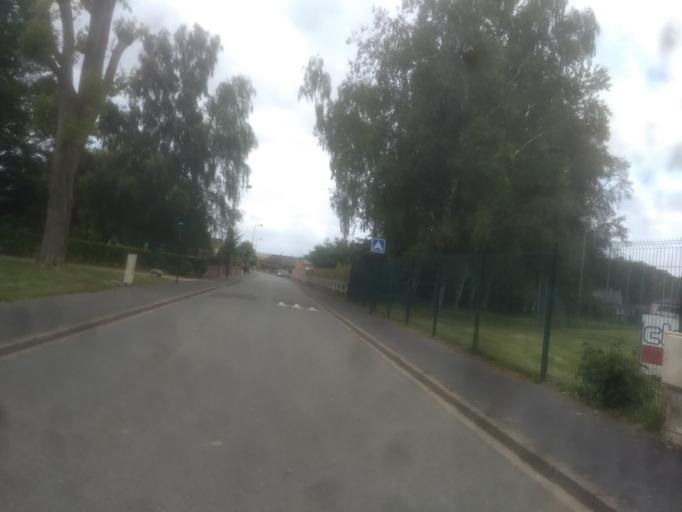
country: FR
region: Nord-Pas-de-Calais
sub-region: Departement du Pas-de-Calais
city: Tilloy-les-Mofflaines
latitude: 50.2715
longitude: 2.8169
